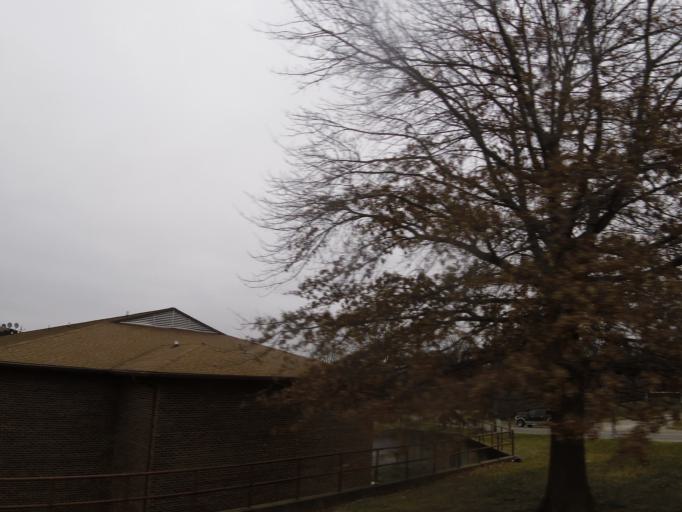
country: US
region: Missouri
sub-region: Marion County
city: Hannibal
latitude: 39.7131
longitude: -91.4004
